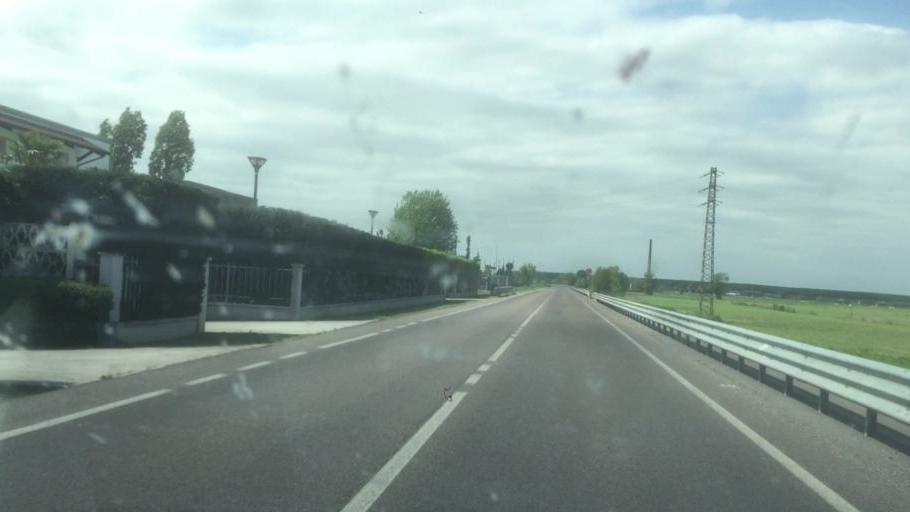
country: IT
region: Veneto
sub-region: Provincia di Rovigo
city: Ceneselli
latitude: 45.0056
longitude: 11.3670
